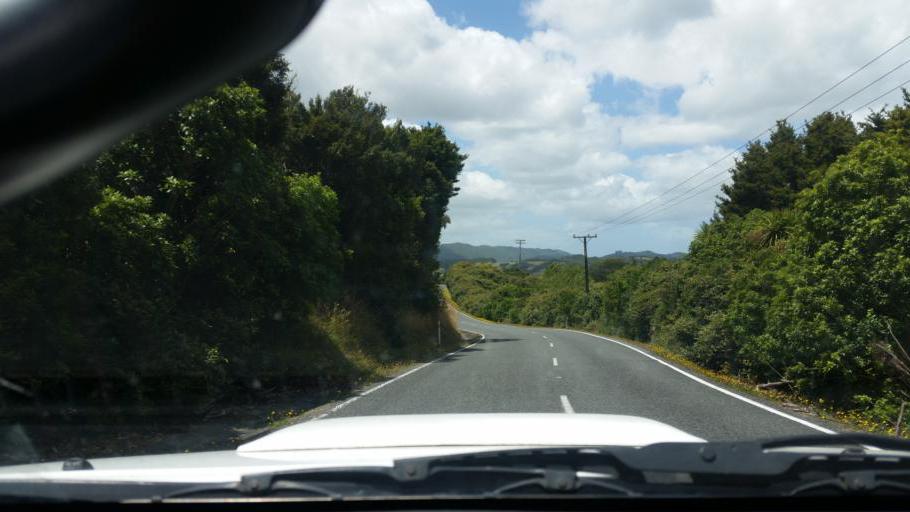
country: NZ
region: Northland
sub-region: Whangarei
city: Ruakaka
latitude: -36.0639
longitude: 174.2693
